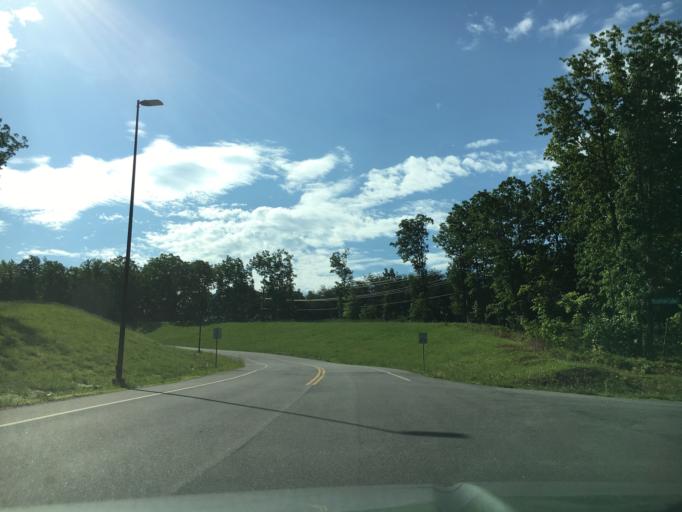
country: US
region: Virginia
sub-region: City of Lynchburg
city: West Lynchburg
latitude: 37.3343
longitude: -79.1845
